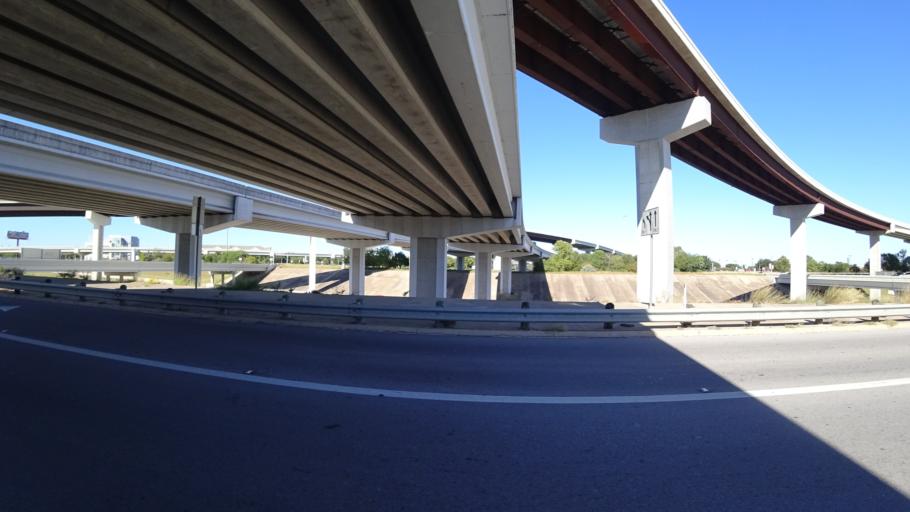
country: US
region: Texas
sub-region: Travis County
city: Rollingwood
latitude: 30.2349
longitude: -97.8248
